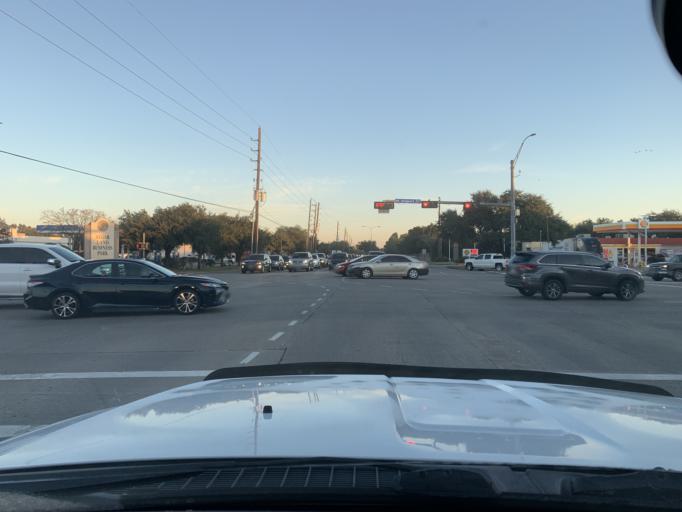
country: US
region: Texas
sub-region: Fort Bend County
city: Meadows Place
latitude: 29.6480
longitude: -95.5978
